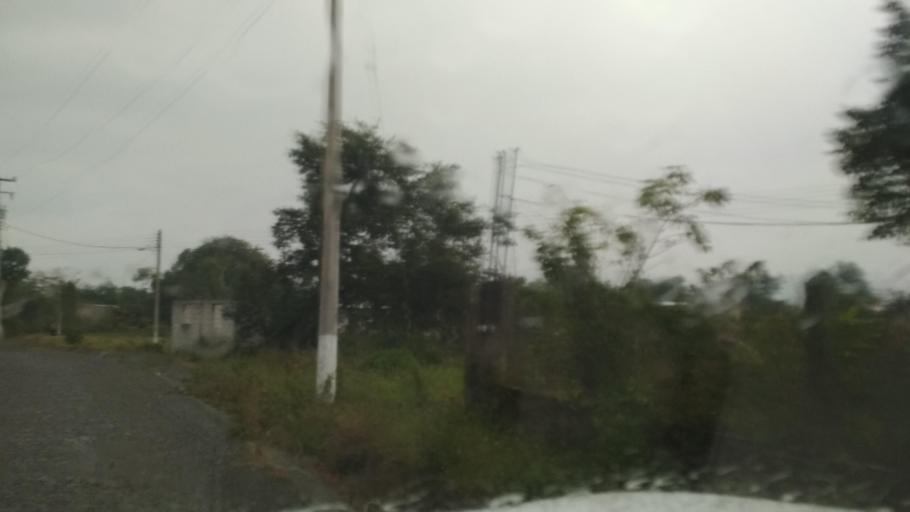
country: MM
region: Shan
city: Taunggyi
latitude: 20.3013
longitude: 97.3059
